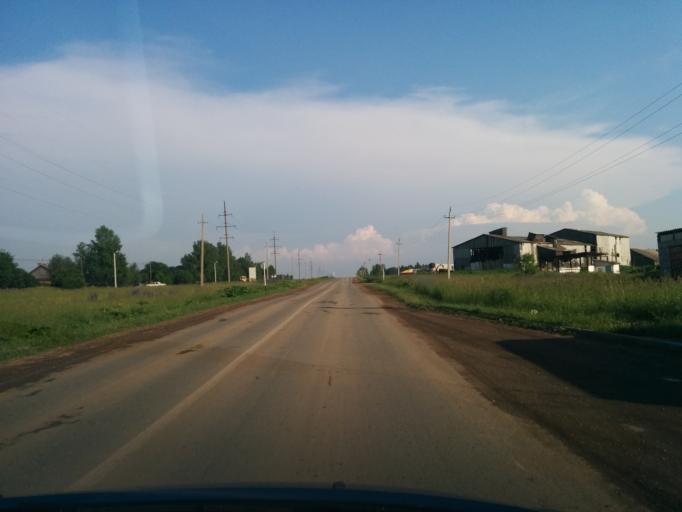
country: RU
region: Perm
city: Polazna
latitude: 58.2298
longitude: 56.2891
